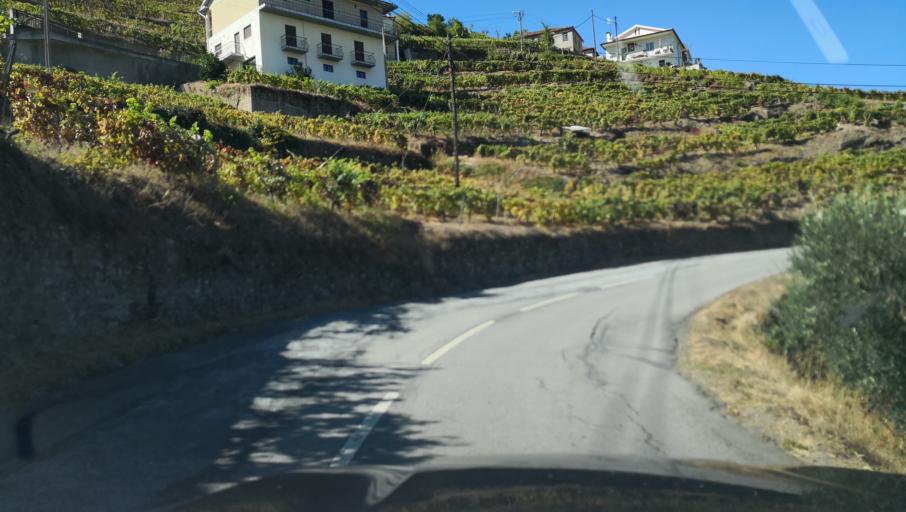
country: PT
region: Vila Real
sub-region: Santa Marta de Penaguiao
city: Santa Marta de Penaguiao
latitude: 41.2264
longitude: -7.7878
